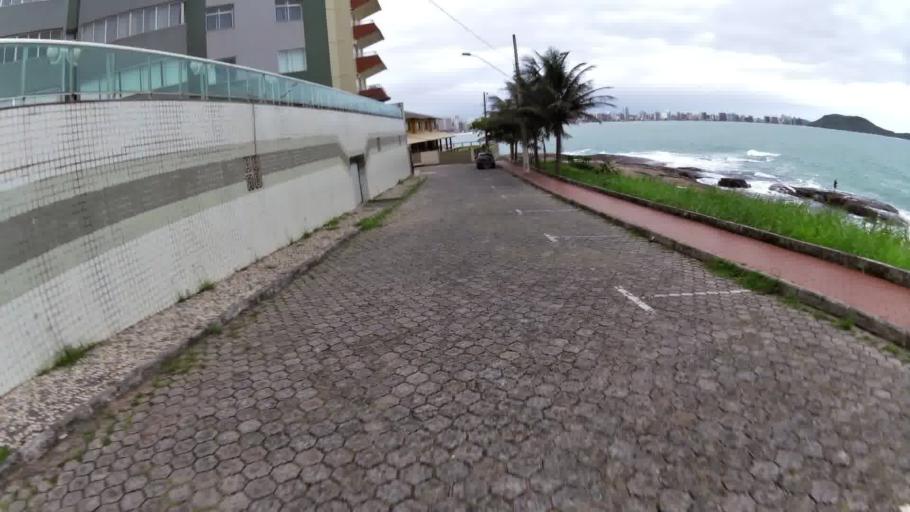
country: BR
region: Espirito Santo
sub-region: Guarapari
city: Guarapari
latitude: -20.6685
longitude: -40.4922
